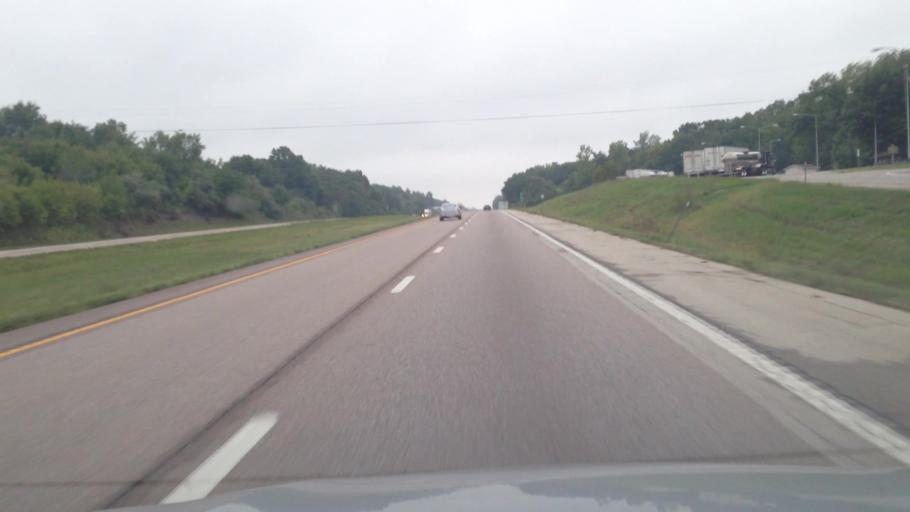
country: US
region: Missouri
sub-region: Clinton County
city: Lathrop
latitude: 39.4835
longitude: -94.3062
